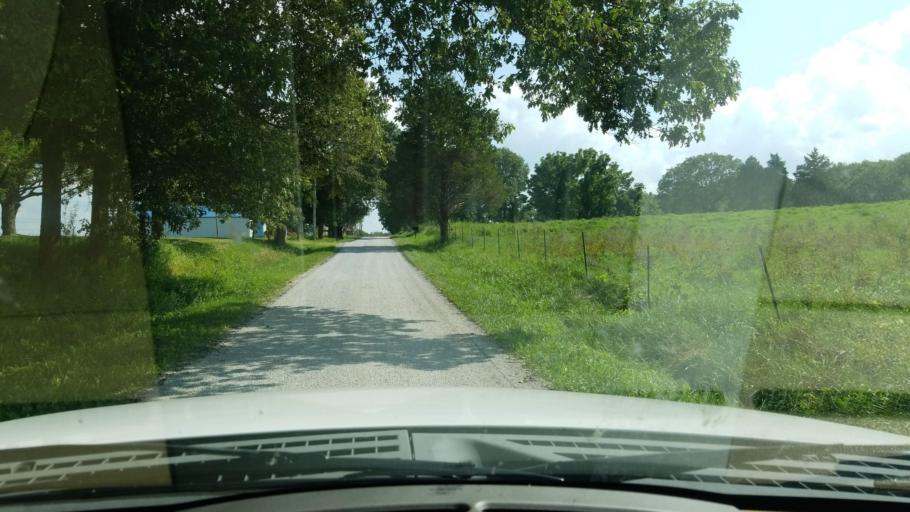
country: US
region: Illinois
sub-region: Saline County
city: Eldorado
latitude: 37.8408
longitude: -88.4810
